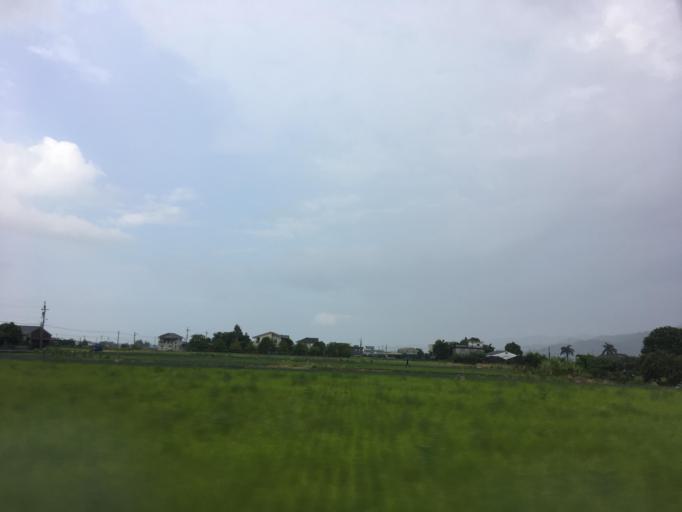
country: TW
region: Taiwan
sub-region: Yilan
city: Yilan
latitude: 24.6697
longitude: 121.6354
